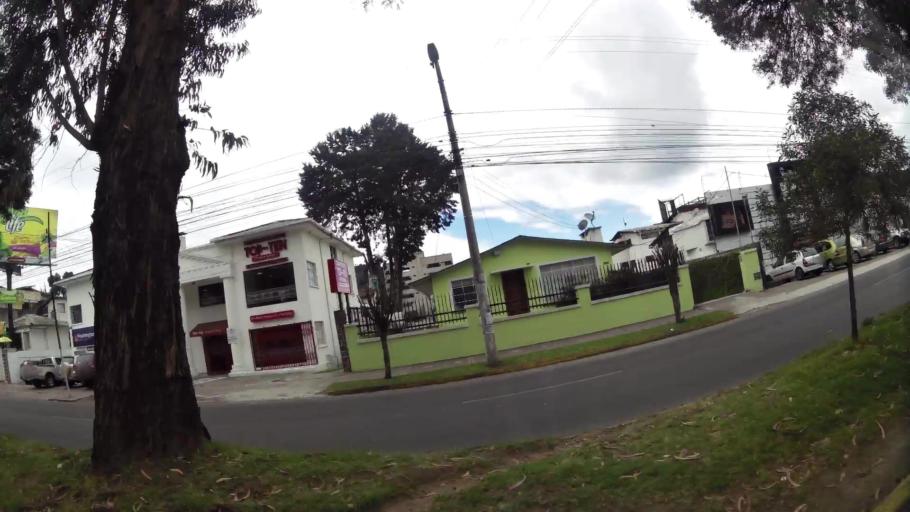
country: EC
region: Pichincha
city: Quito
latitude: -0.1700
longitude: -78.4904
